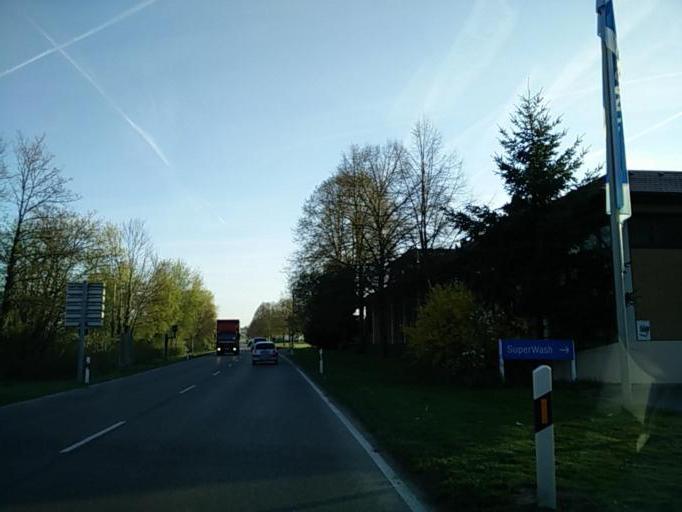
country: DE
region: Baden-Wuerttemberg
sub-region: Regierungsbezirk Stuttgart
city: Herrenberg
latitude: 48.6007
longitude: 8.8728
